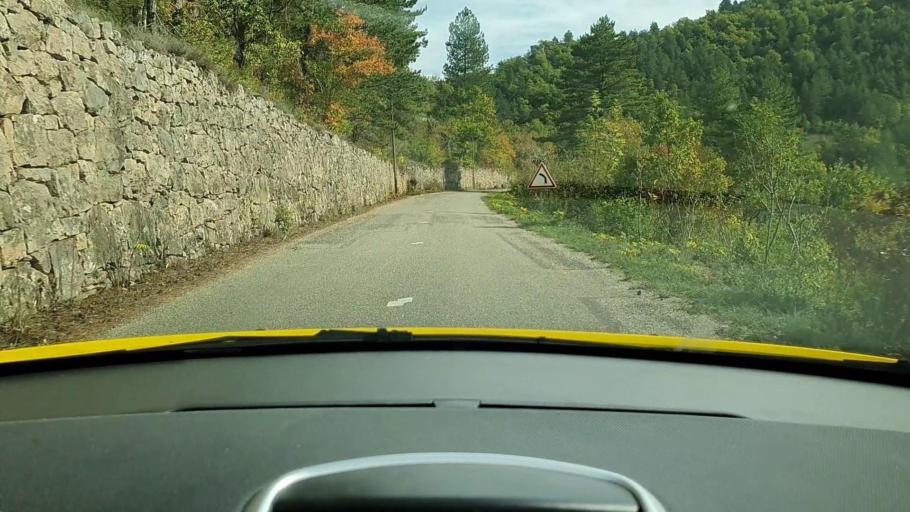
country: FR
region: Languedoc-Roussillon
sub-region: Departement de la Lozere
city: Meyrueis
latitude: 44.0772
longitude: 3.3737
